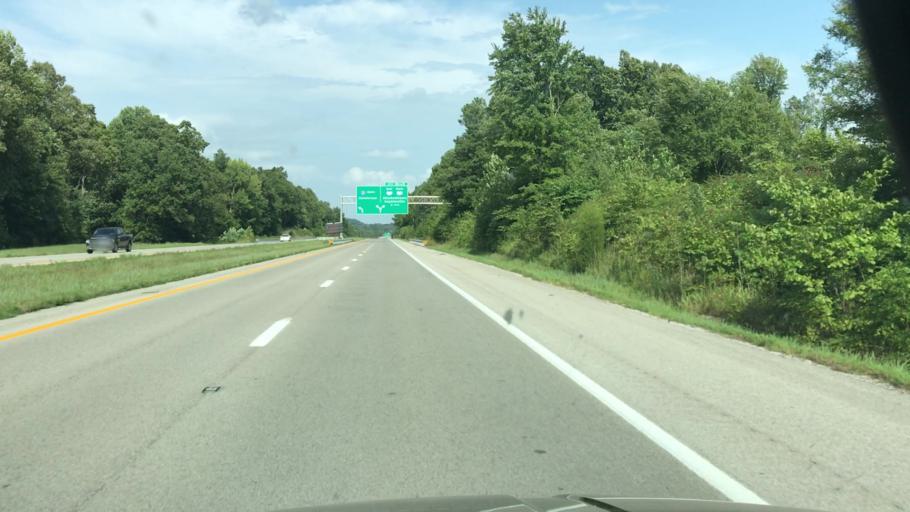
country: US
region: Kentucky
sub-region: Hopkins County
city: Nortonville
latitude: 37.2086
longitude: -87.4911
